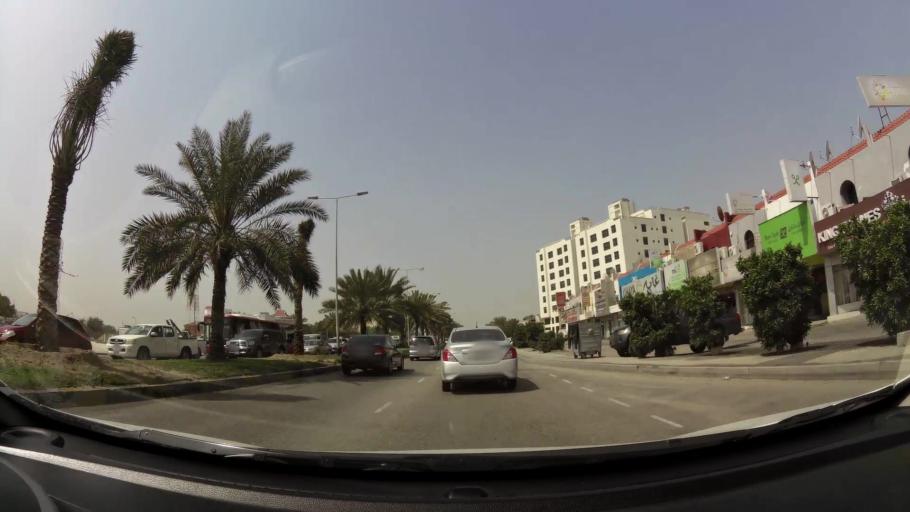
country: BH
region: Manama
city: Jidd Hafs
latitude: 26.2206
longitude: 50.5049
